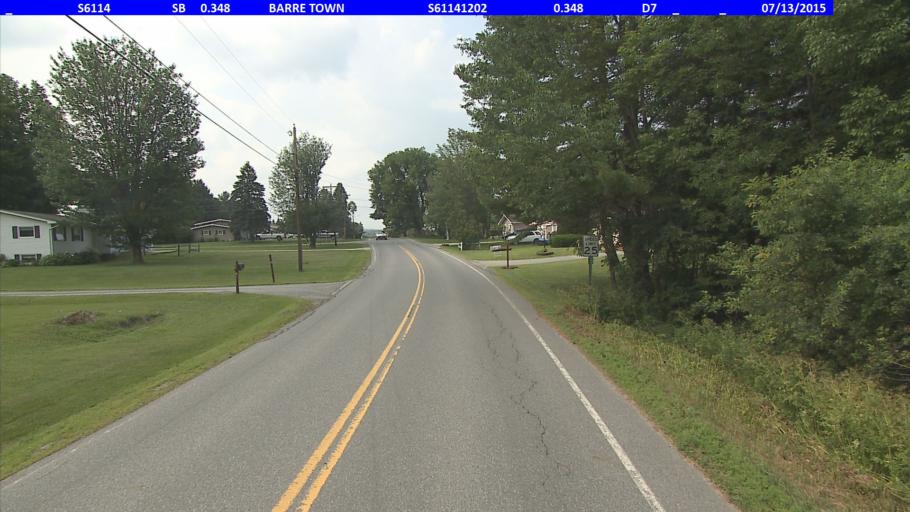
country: US
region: Vermont
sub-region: Washington County
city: Barre
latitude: 44.1965
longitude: -72.4787
